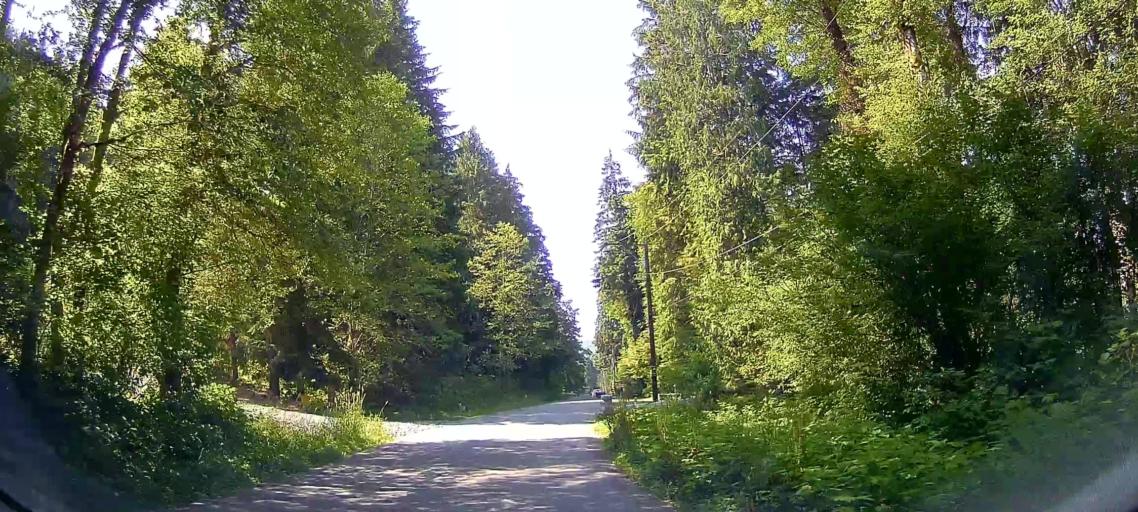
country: US
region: Washington
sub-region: Snohomish County
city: Arlington Heights
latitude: 48.3181
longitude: -122.0263
